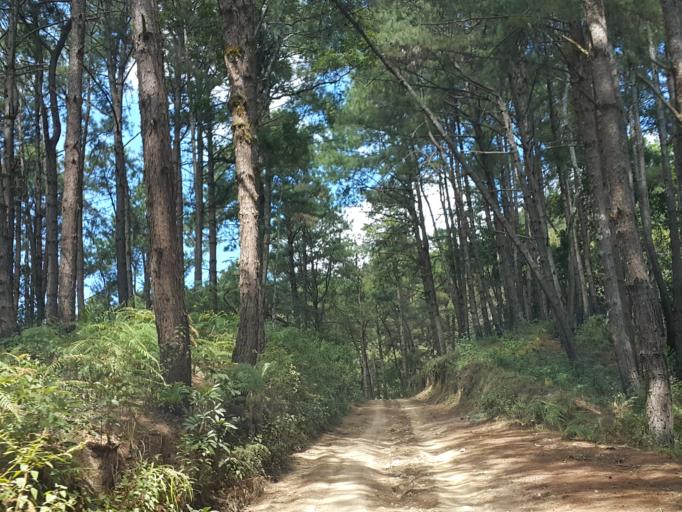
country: TH
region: Chiang Mai
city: Wiang Haeng
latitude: 19.5489
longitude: 98.8142
